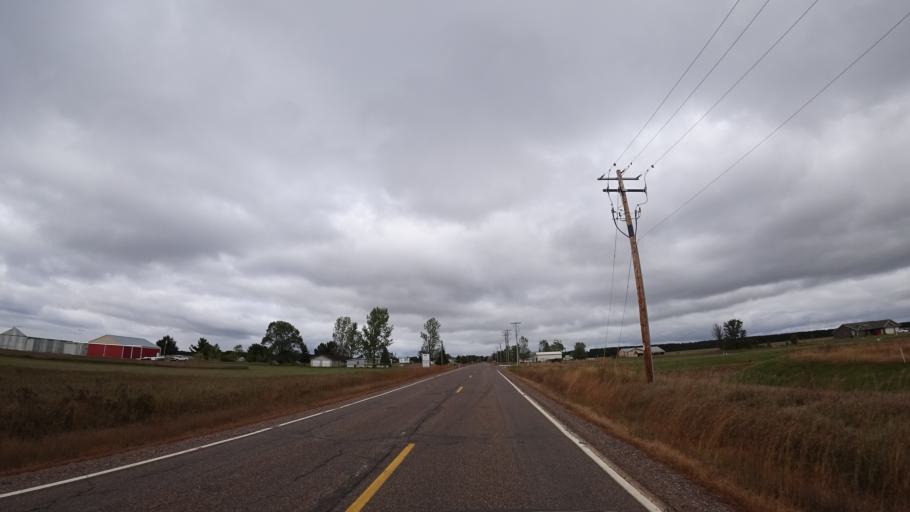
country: US
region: Wisconsin
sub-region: Chippewa County
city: Lake Wissota
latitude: 44.9351
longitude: -91.2678
